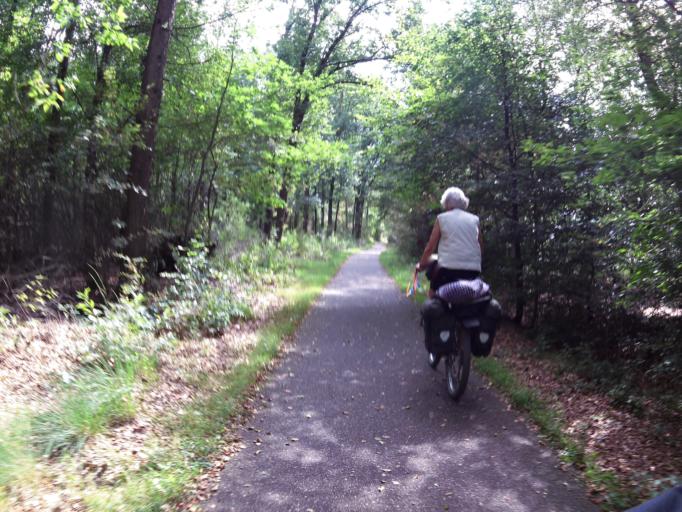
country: NL
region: Drenthe
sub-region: Gemeente Borger-Odoorn
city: Borger
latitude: 52.9414
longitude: 6.7518
